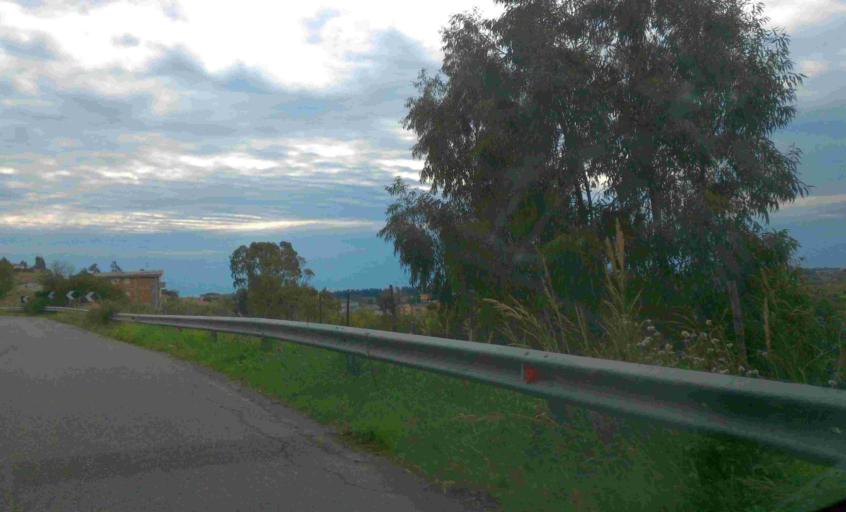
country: IT
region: Calabria
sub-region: Provincia di Catanzaro
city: Sellia Marina
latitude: 38.8896
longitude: 16.7071
